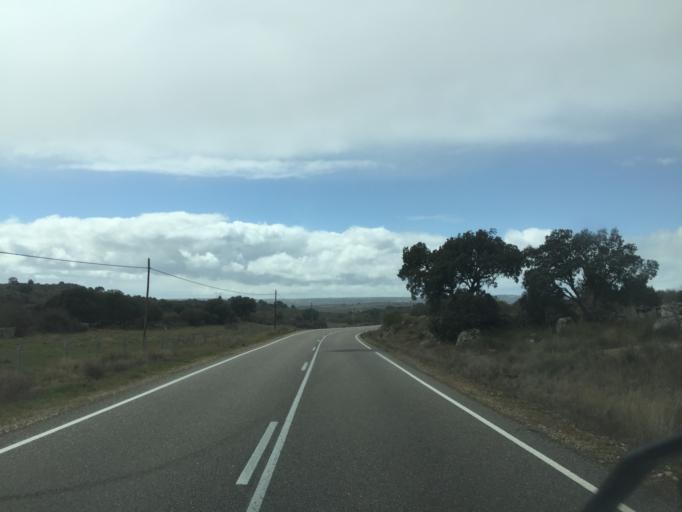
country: ES
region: Castille and Leon
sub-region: Provincia de Zamora
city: Villalcampo
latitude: 41.5132
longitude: -6.0630
